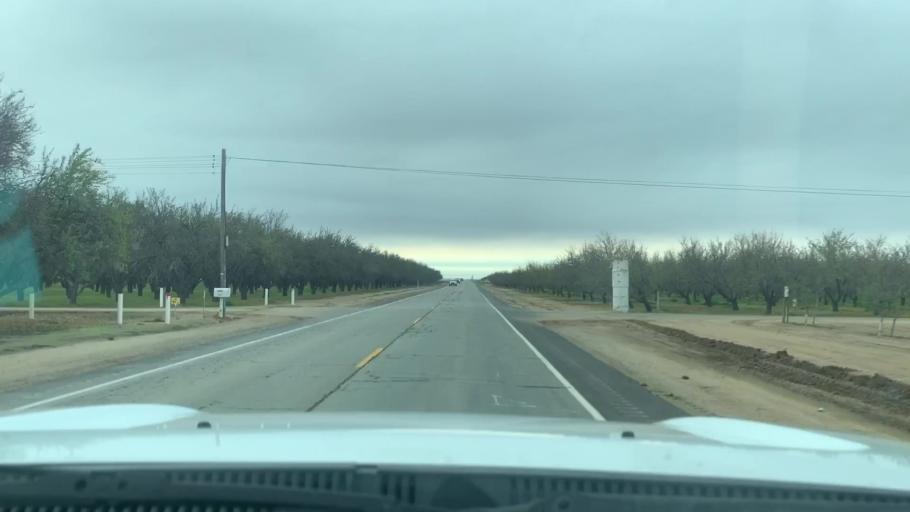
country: US
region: California
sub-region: Kern County
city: Rosedale
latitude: 35.4780
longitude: -119.1532
